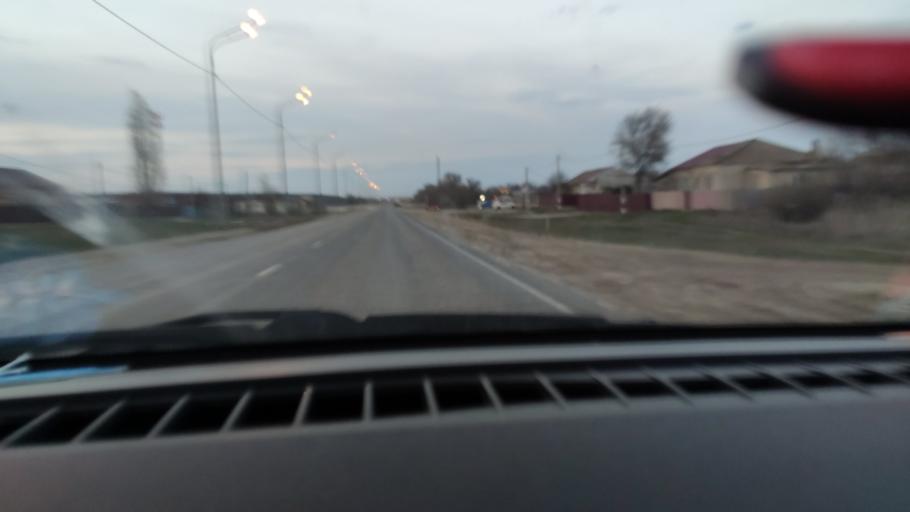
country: RU
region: Saratov
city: Sinodskoye
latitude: 51.9980
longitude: 46.6755
